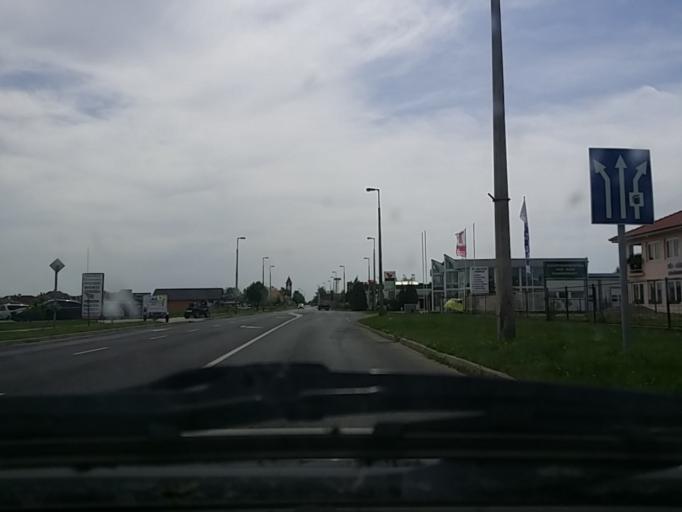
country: HU
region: Somogy
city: Barcs
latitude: 45.9660
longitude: 17.4663
